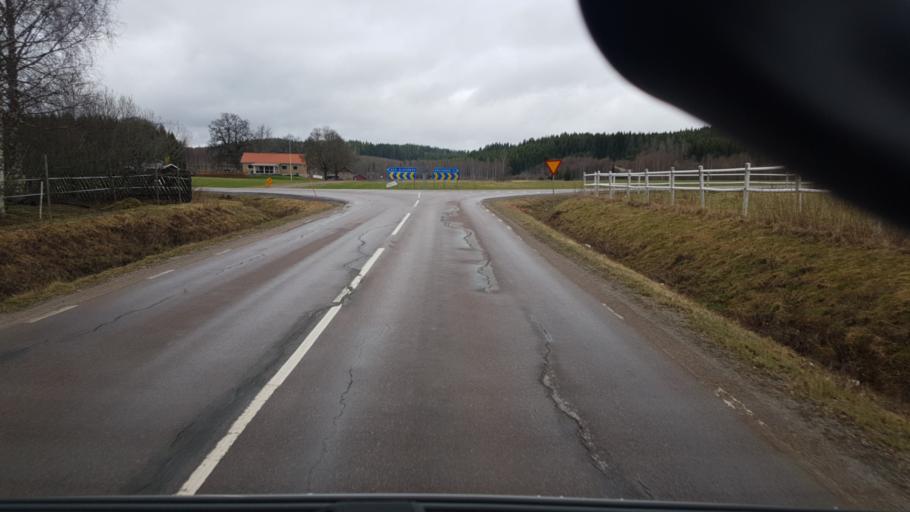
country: SE
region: Vaermland
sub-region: Eda Kommun
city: Charlottenberg
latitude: 59.9216
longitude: 12.2855
